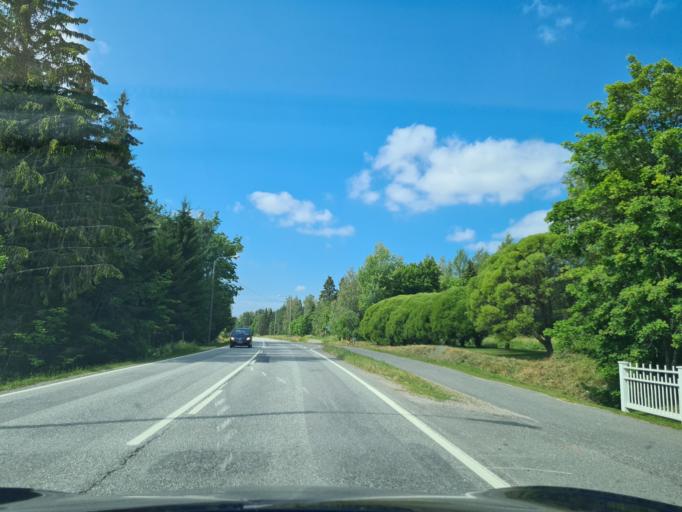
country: FI
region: Ostrobothnia
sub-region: Vaasa
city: Vaasa
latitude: 63.1925
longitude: 21.5604
